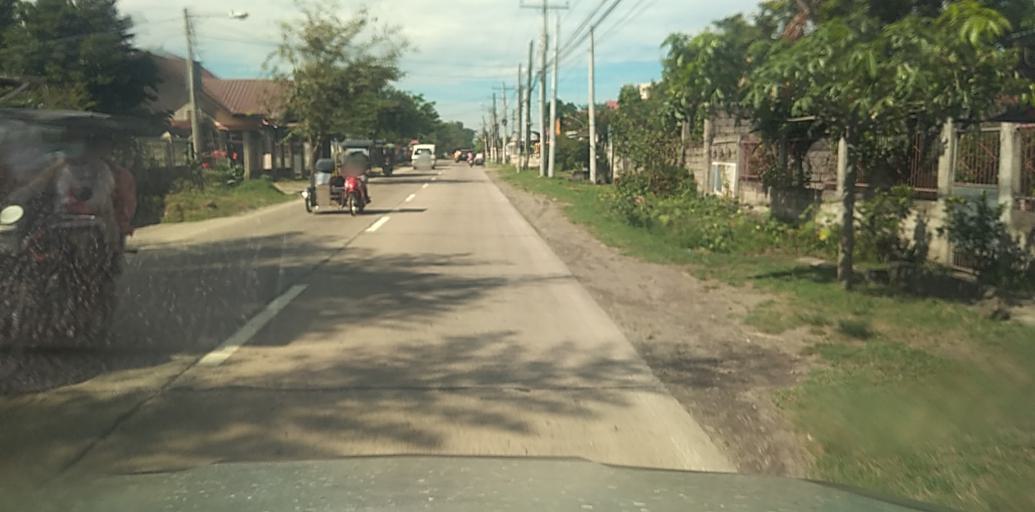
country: PH
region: Central Luzon
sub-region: Province of Pampanga
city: Arayat
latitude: 15.1536
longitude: 120.7299
